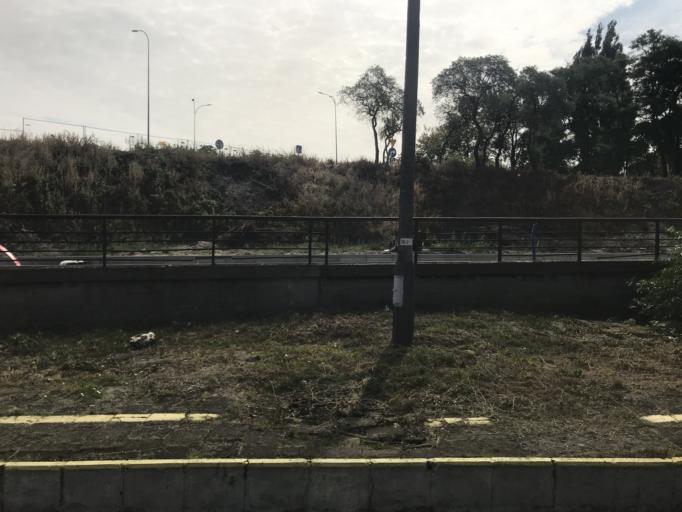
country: PL
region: Kujawsko-Pomorskie
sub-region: Powiat inowroclawski
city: Inowroclaw
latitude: 52.8070
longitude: 18.2447
